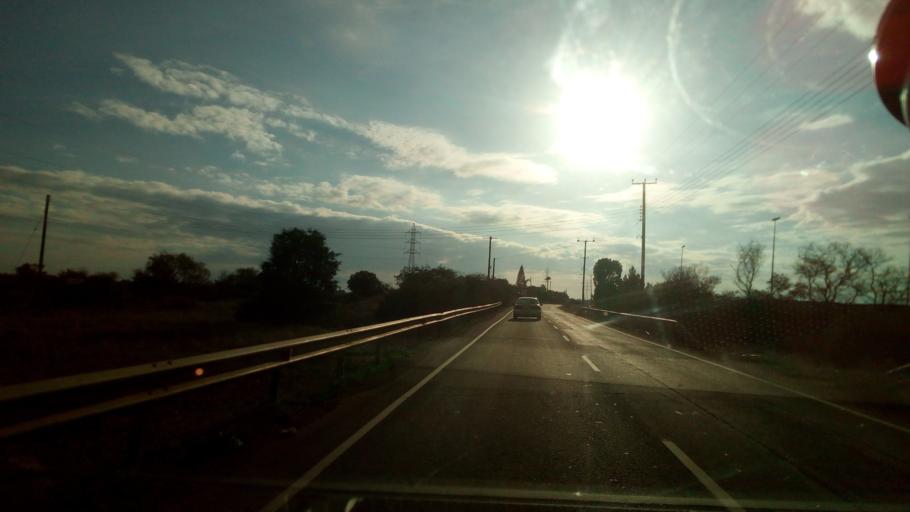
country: CY
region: Ammochostos
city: Avgorou
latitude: 35.0213
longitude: 33.8304
